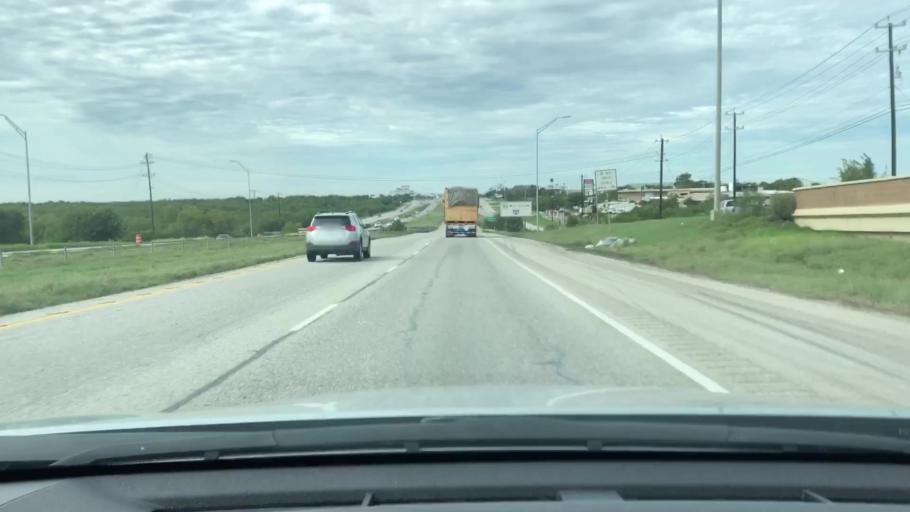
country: US
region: Texas
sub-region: Bexar County
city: Kirby
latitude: 29.4435
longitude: -98.3661
